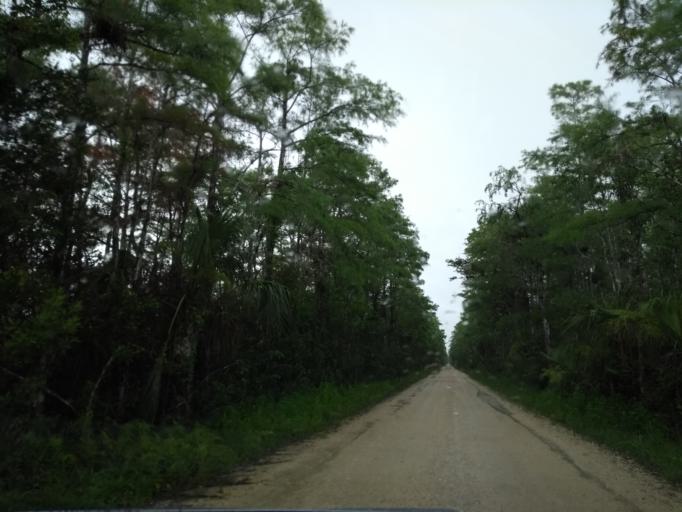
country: US
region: Florida
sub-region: Miami-Dade County
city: The Hammocks
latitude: 25.7602
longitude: -81.0457
